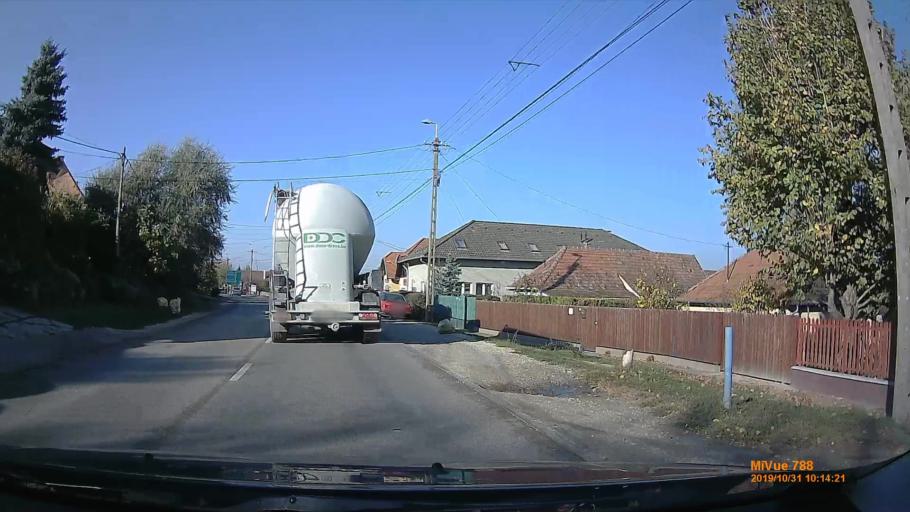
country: HU
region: Pest
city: Pecel
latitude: 47.4920
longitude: 19.3186
